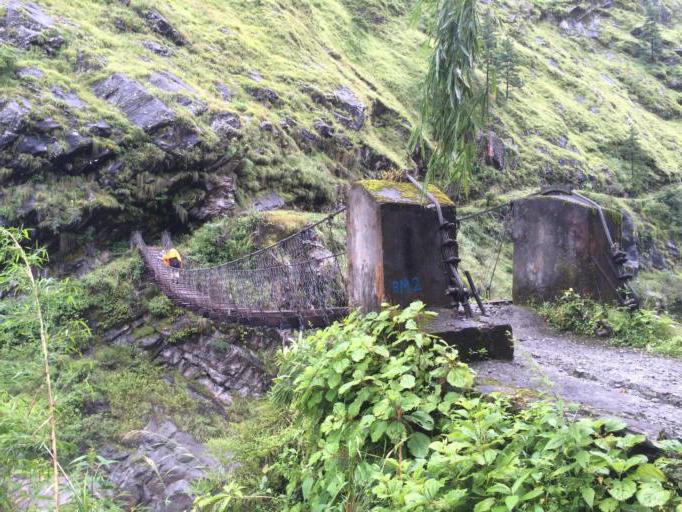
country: NP
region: Western Region
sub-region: Dhawalagiri Zone
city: Chitre
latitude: 28.5927
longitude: 83.6461
